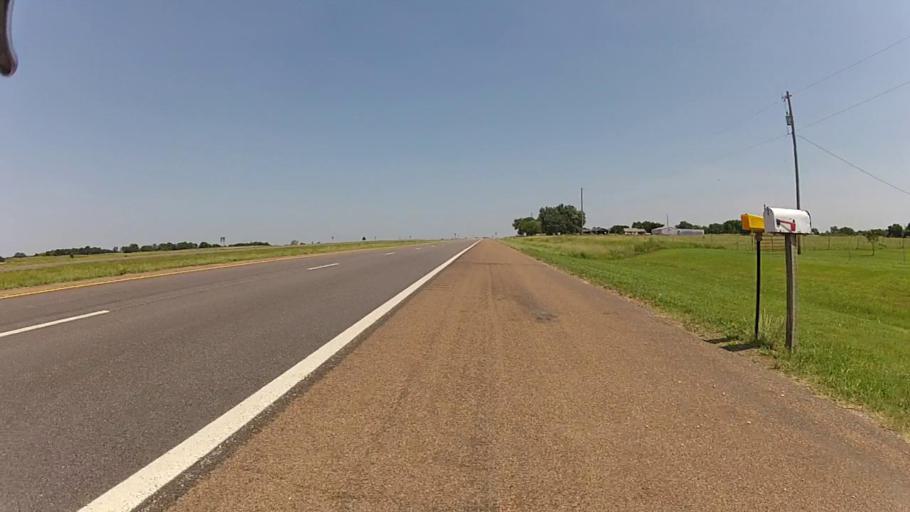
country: US
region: Kansas
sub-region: Montgomery County
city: Cherryvale
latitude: 37.2274
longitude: -95.5856
